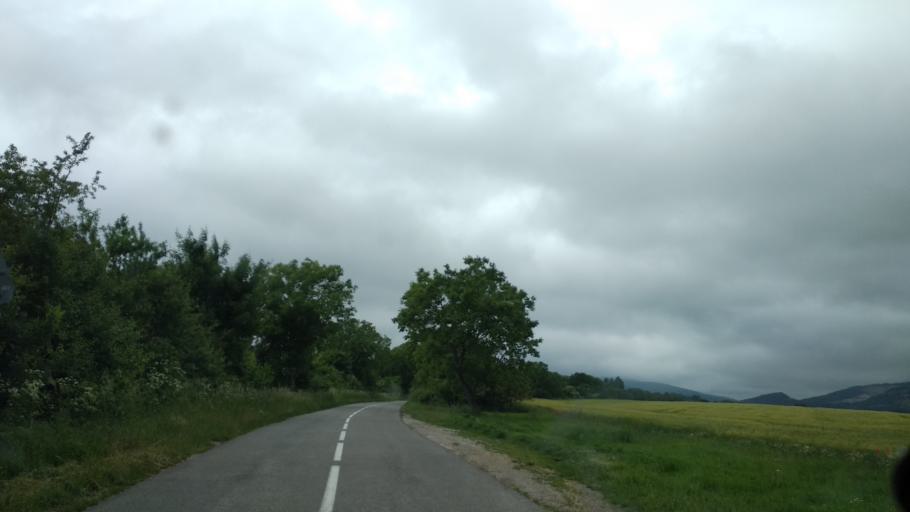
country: SK
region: Nitriansky
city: Trencianske Teplice
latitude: 48.7878
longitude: 18.1452
